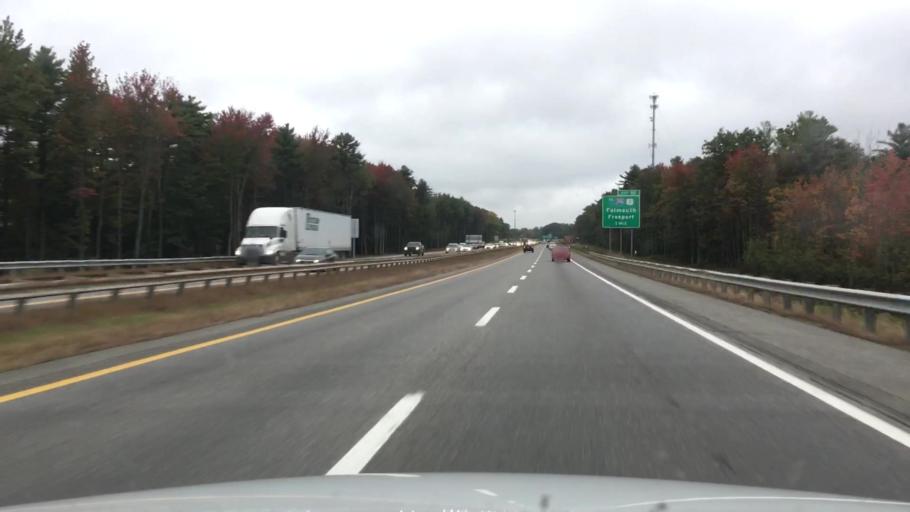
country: US
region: Maine
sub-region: Cumberland County
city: Westbrook
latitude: 43.7022
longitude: -70.3141
